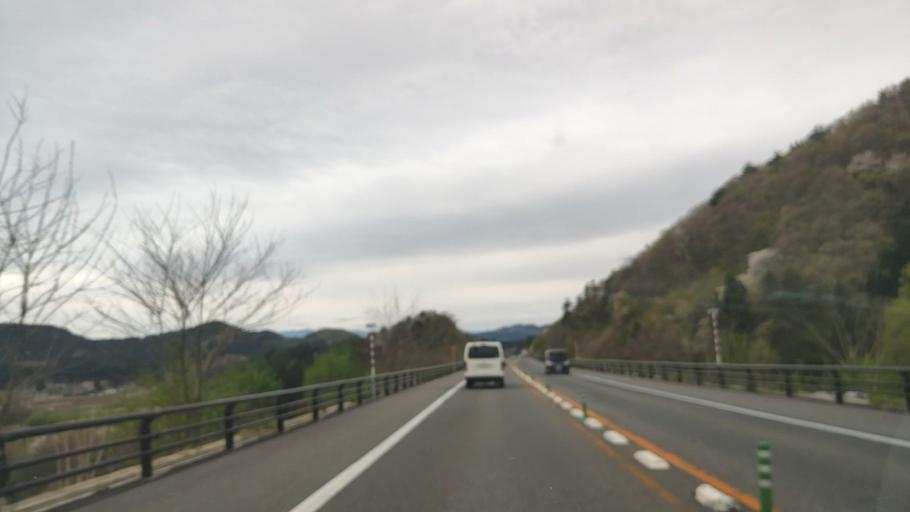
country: JP
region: Akita
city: Odate
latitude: 40.3216
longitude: 140.5958
